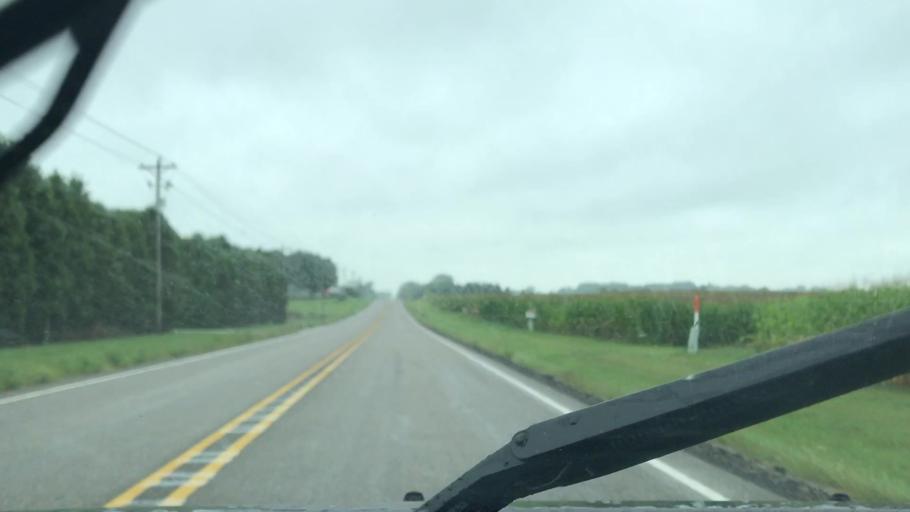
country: US
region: Indiana
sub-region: Boone County
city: Lebanon
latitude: 40.1265
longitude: -86.4238
